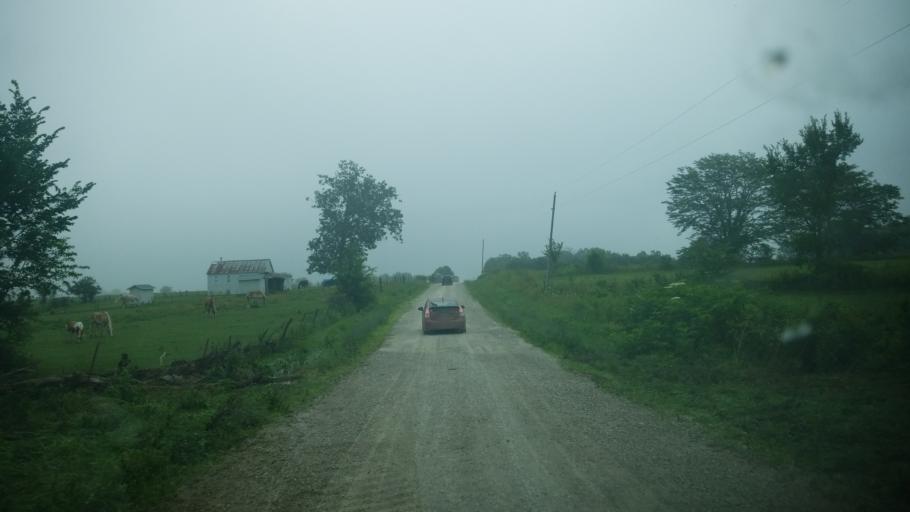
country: US
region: Missouri
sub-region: Pike County
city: Bowling Green
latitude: 39.3088
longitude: -91.3240
